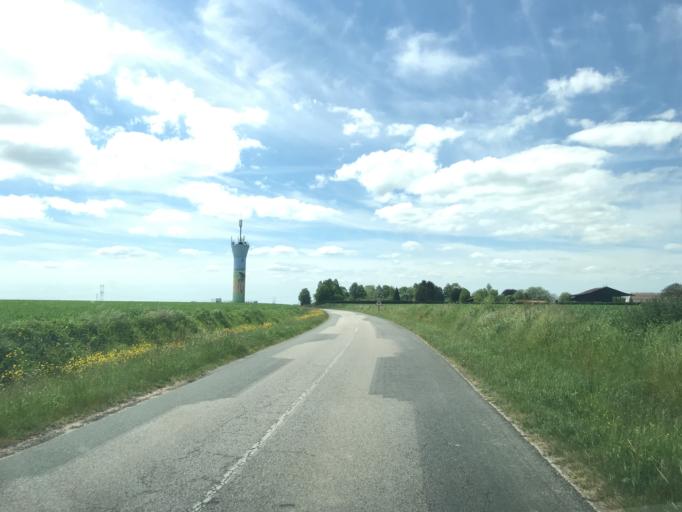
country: FR
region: Haute-Normandie
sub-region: Departement de l'Eure
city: Le Neubourg
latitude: 49.1486
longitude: 0.8679
